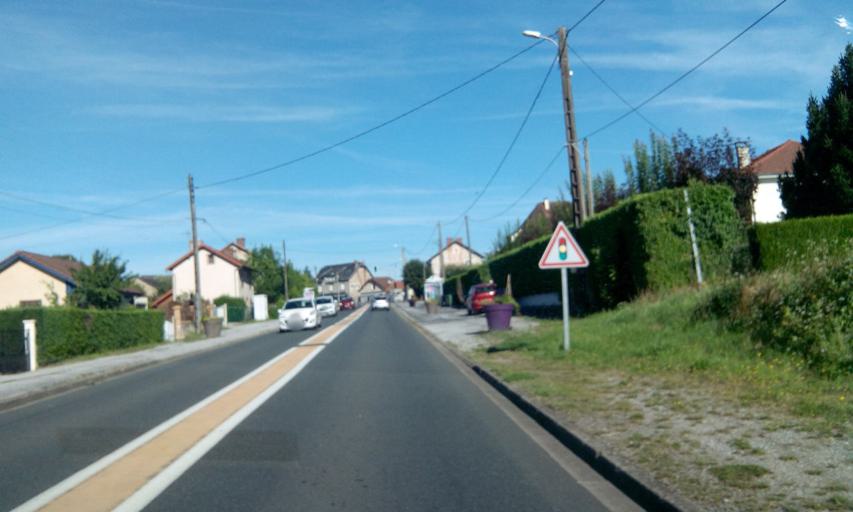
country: FR
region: Limousin
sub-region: Departement de la Haute-Vienne
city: Saint-Just-le-Martel
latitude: 45.8481
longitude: 1.4316
